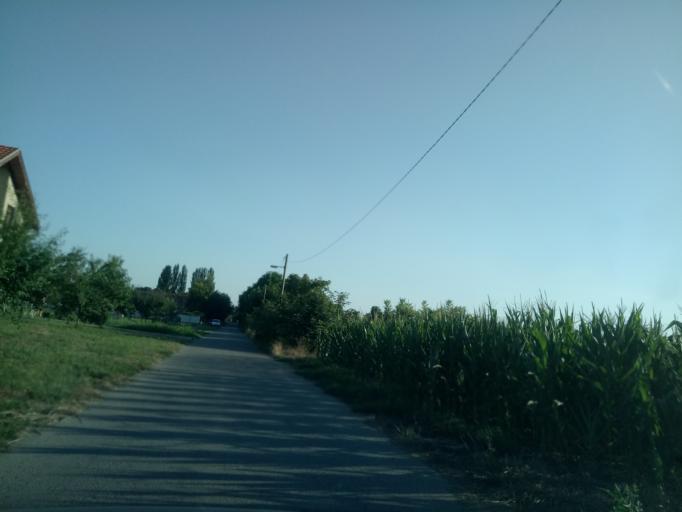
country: RS
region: Autonomna Pokrajina Vojvodina
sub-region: Sremski Okrug
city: Stara Pazova
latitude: 44.9949
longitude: 20.1672
